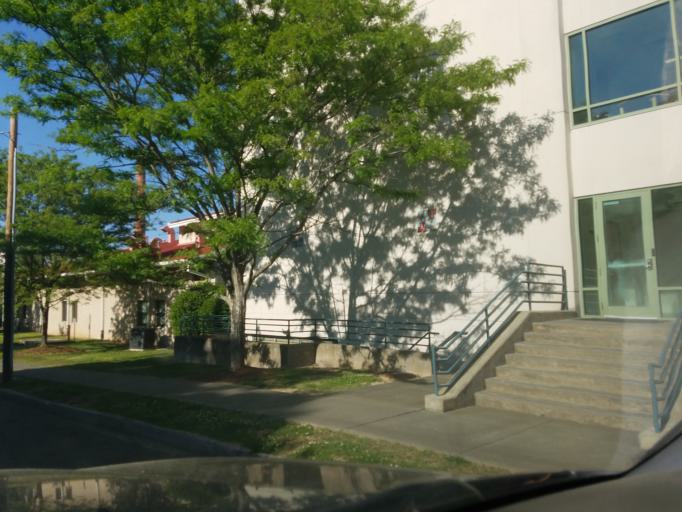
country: US
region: North Carolina
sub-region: Durham County
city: Durham
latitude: 36.0187
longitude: -78.9222
